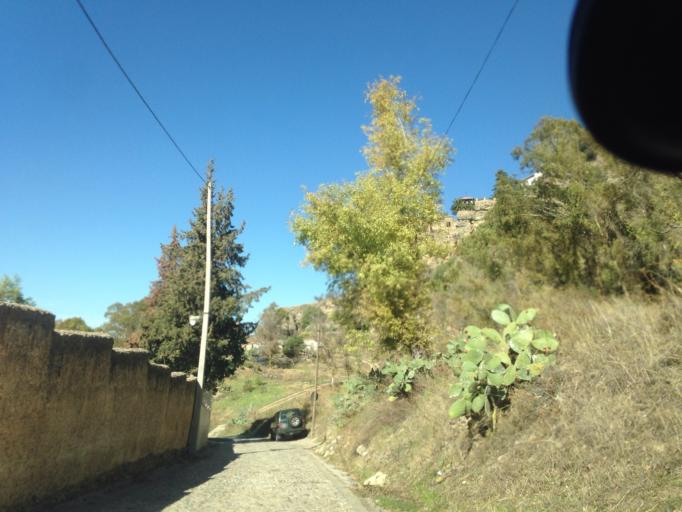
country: ES
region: Andalusia
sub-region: Provincia de Malaga
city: Ronda
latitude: 36.7359
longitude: -5.1664
